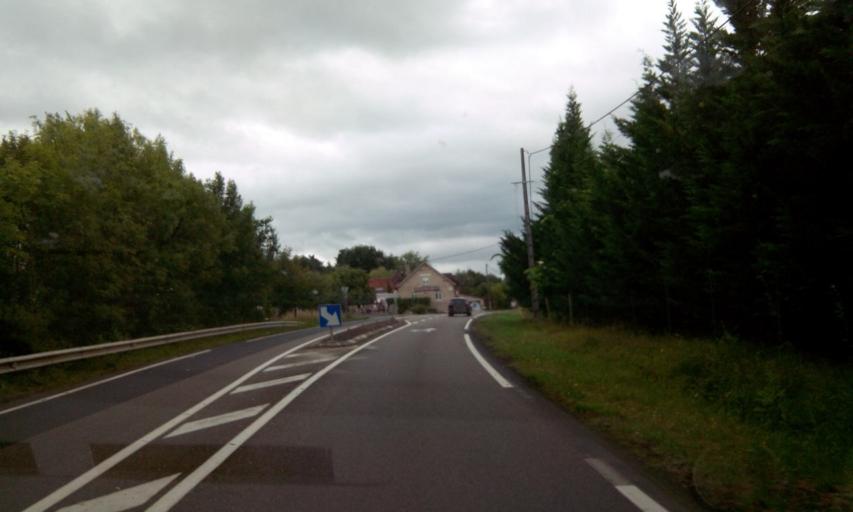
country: FR
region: Limousin
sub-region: Departement de la Correze
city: Cosnac
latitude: 45.1044
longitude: 1.5723
